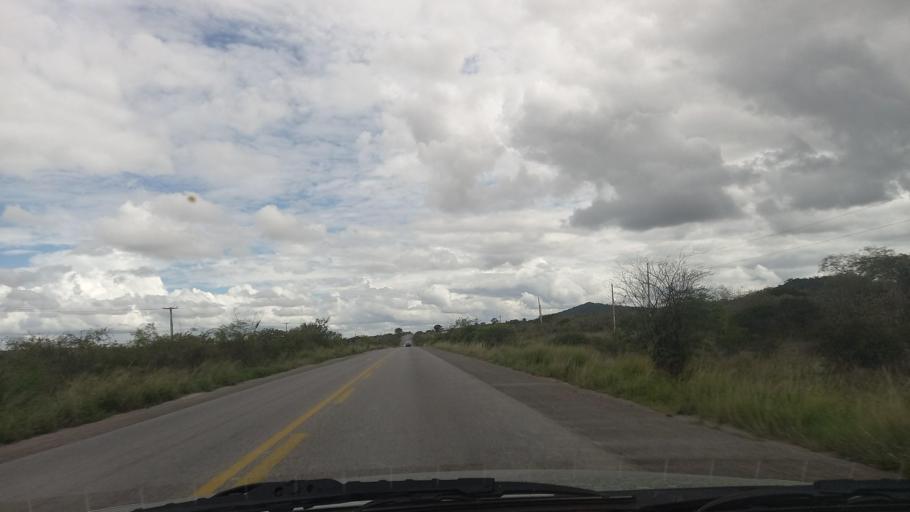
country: BR
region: Pernambuco
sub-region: Cachoeirinha
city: Cachoeirinha
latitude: -8.3381
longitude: -36.1582
